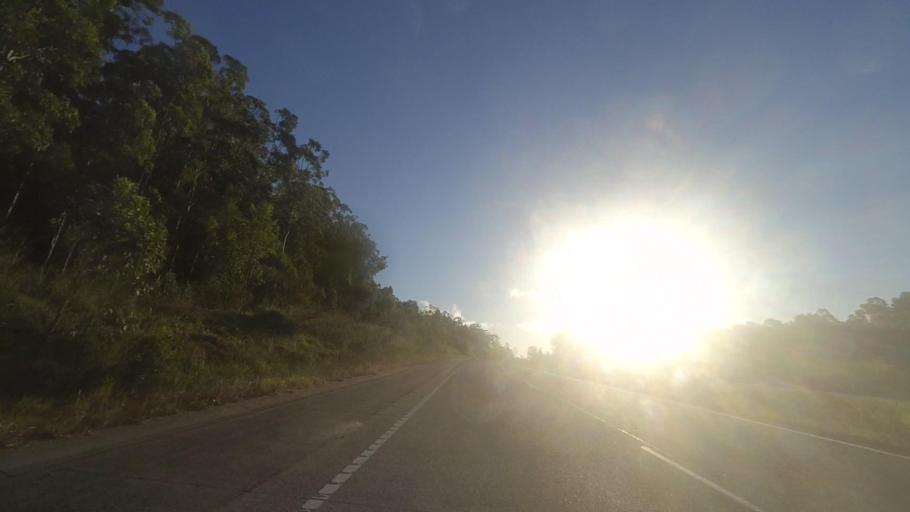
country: AU
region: New South Wales
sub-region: Great Lakes
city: Bulahdelah
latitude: -32.5335
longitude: 152.1811
